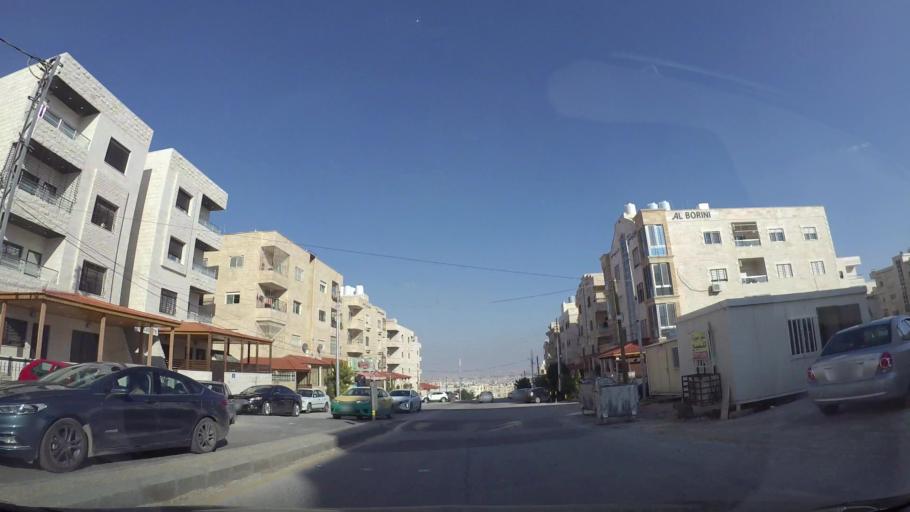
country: JO
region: Amman
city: Amman
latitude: 31.9870
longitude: 35.9393
